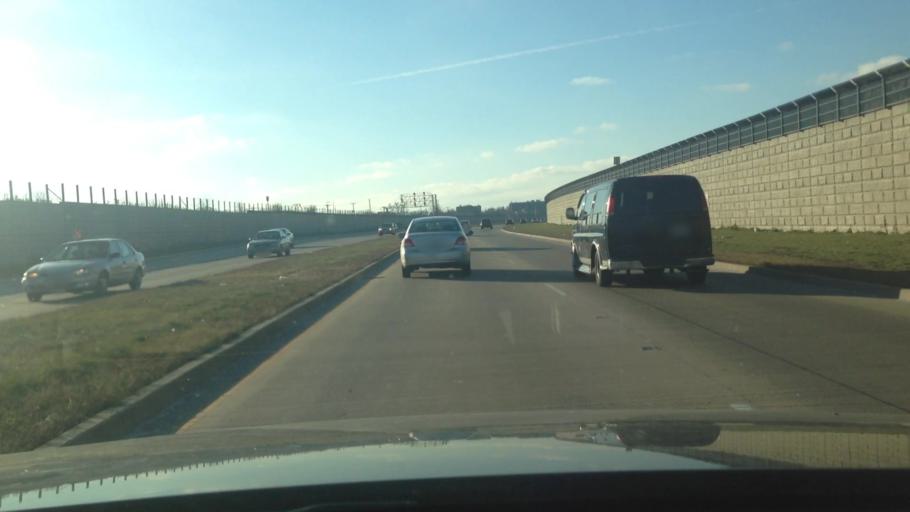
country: US
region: Illinois
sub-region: DuPage County
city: Bensenville
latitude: 41.9553
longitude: -87.9254
